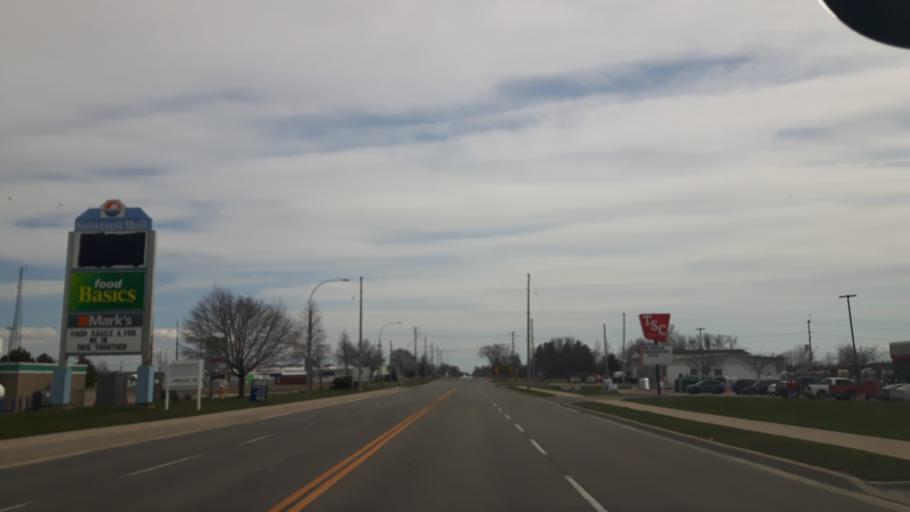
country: CA
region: Ontario
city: Goderich
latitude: 43.7298
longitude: -81.7060
